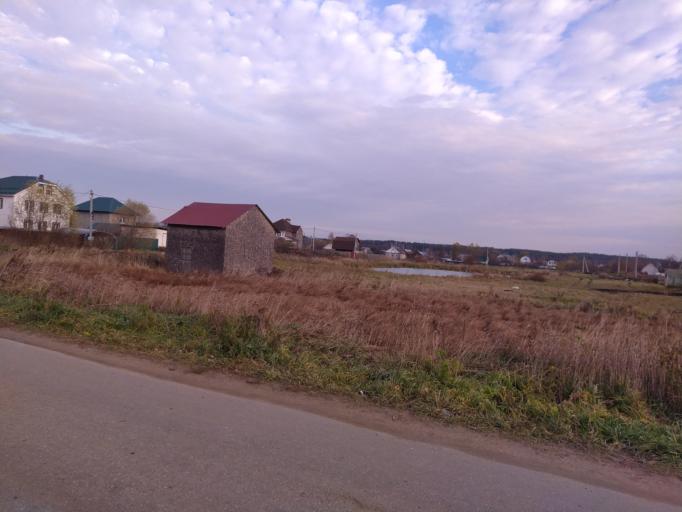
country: RU
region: Moskovskaya
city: Kolomna
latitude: 55.1417
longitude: 38.7924
